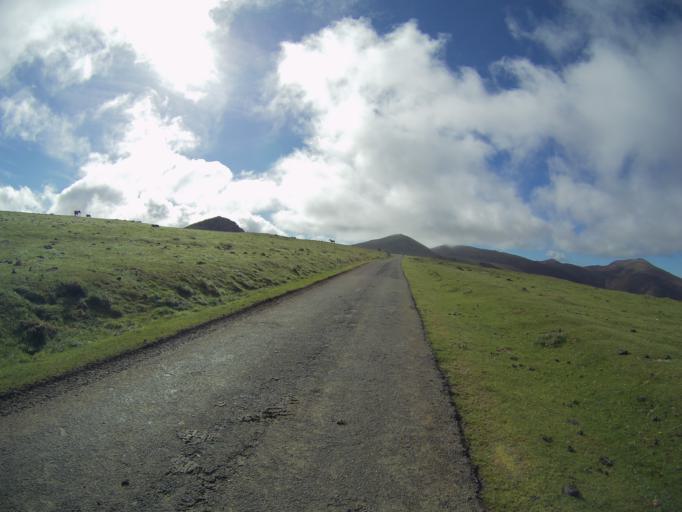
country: FR
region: Aquitaine
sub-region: Departement des Pyrenees-Atlantiques
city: Saint-Jean-Pied-de-Port
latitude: 43.0696
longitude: -1.2694
